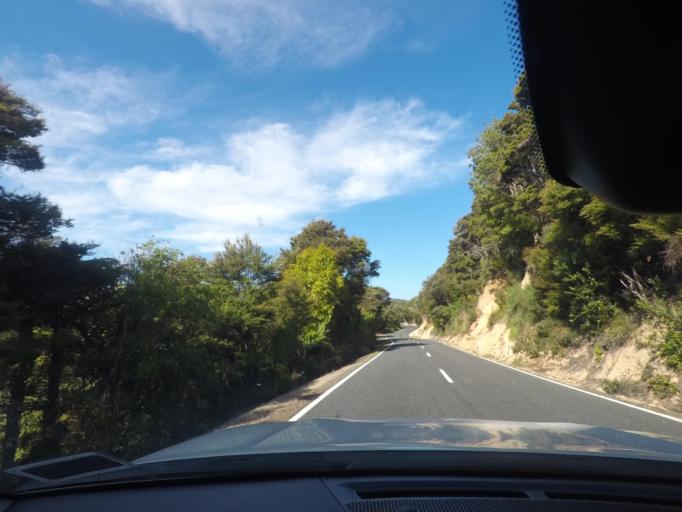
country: NZ
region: Northland
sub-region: Whangarei
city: Ngunguru
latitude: -35.6650
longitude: 174.4783
